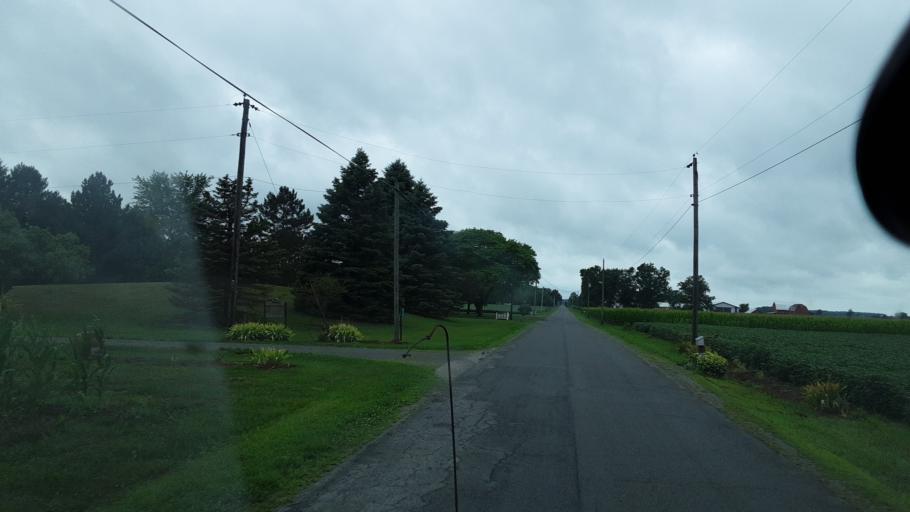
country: US
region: Ohio
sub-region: Van Wert County
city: Convoy
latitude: 40.8224
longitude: -84.7117
